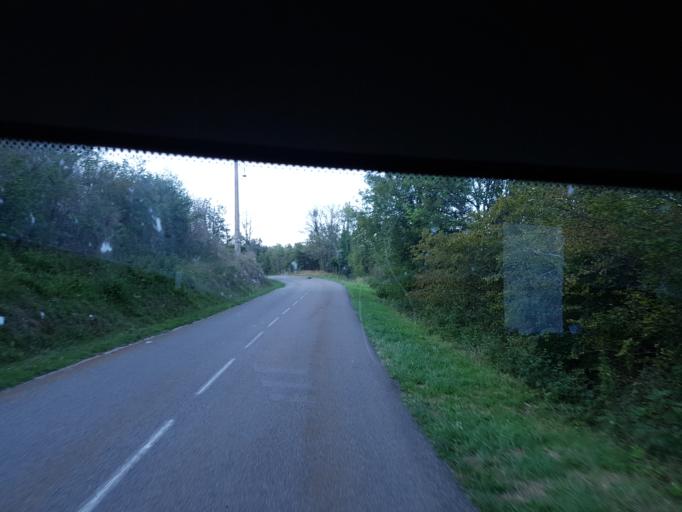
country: FR
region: Franche-Comte
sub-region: Departement du Jura
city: Moirans-en-Montagne
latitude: 46.4131
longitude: 5.6491
